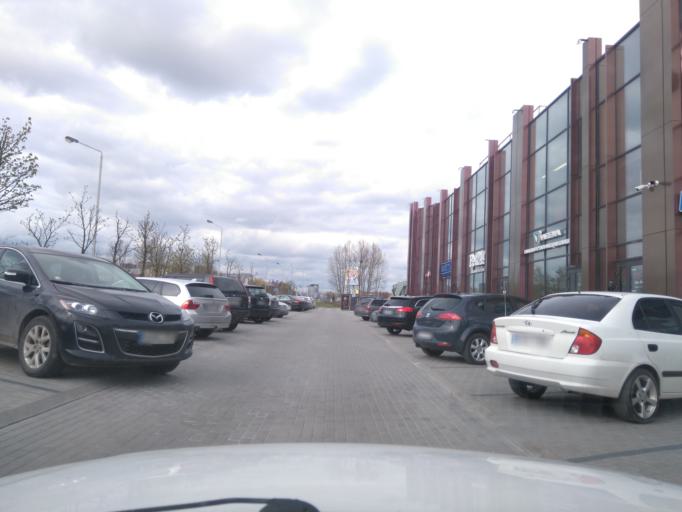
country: LT
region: Kauno apskritis
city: Dainava (Kaunas)
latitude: 54.9063
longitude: 23.9810
